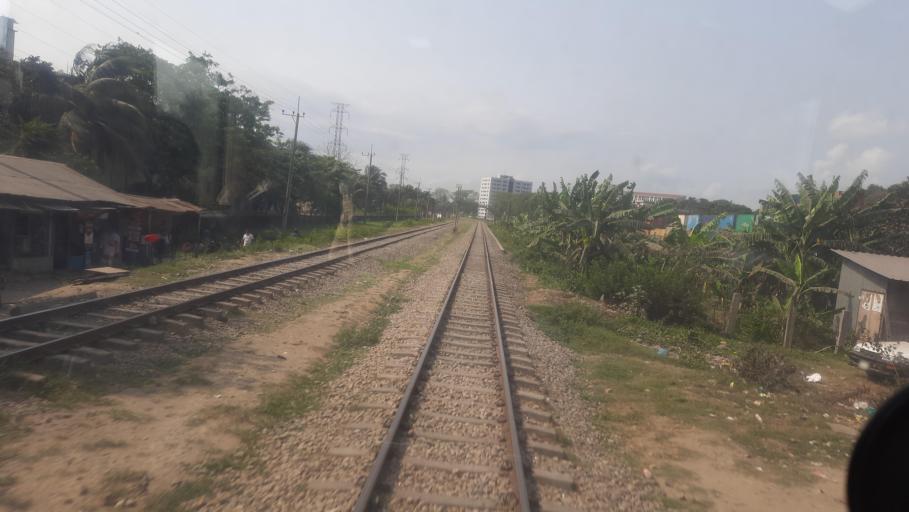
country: BD
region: Chittagong
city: Chittagong
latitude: 22.4164
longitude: 91.7542
